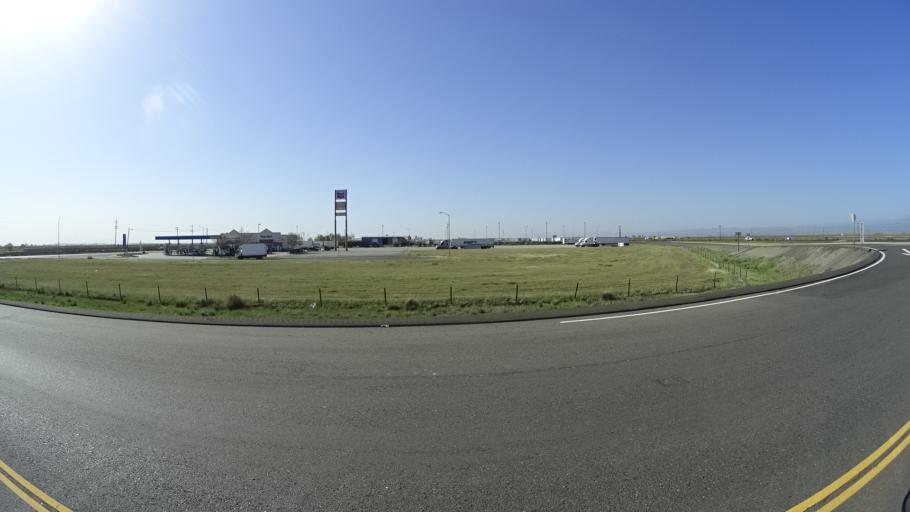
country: US
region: California
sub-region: Glenn County
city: Willows
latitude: 39.4951
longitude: -122.1945
